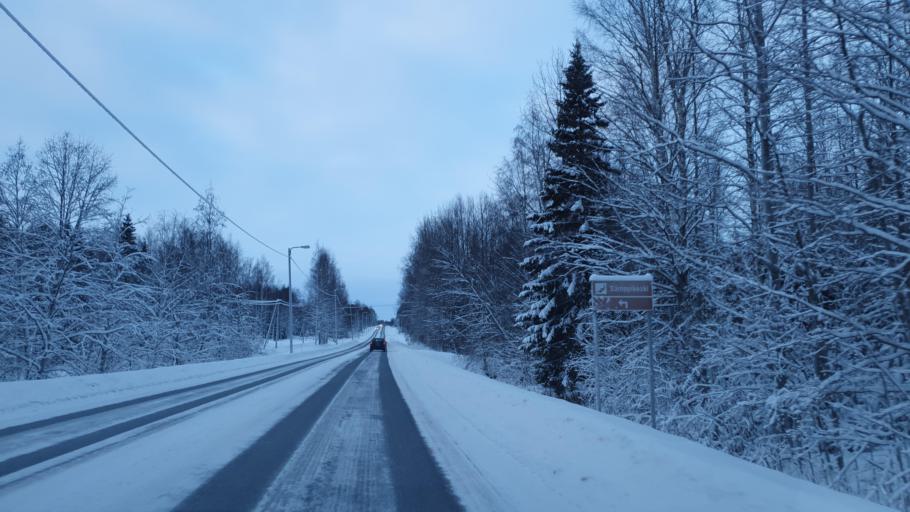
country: FI
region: Northern Ostrobothnia
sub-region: Oulu
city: Haukipudas
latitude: 65.1978
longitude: 25.3894
